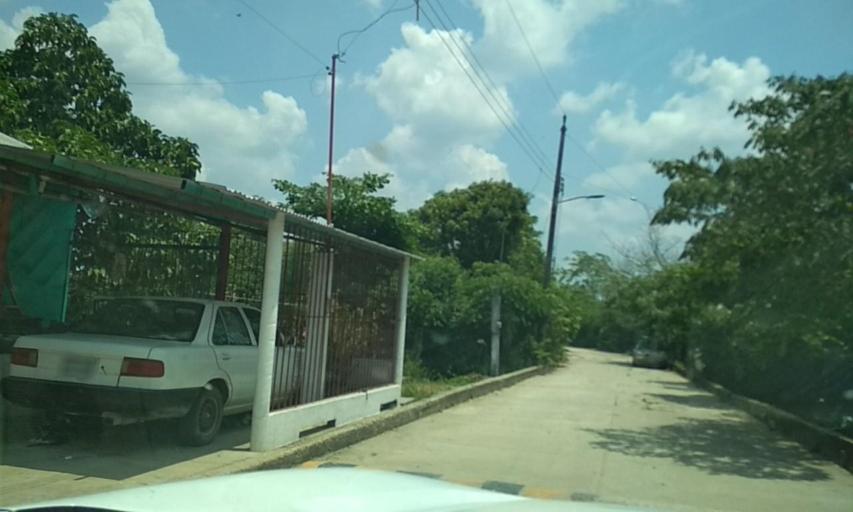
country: MX
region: Veracruz
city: Las Choapas
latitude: 17.9135
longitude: -94.0856
